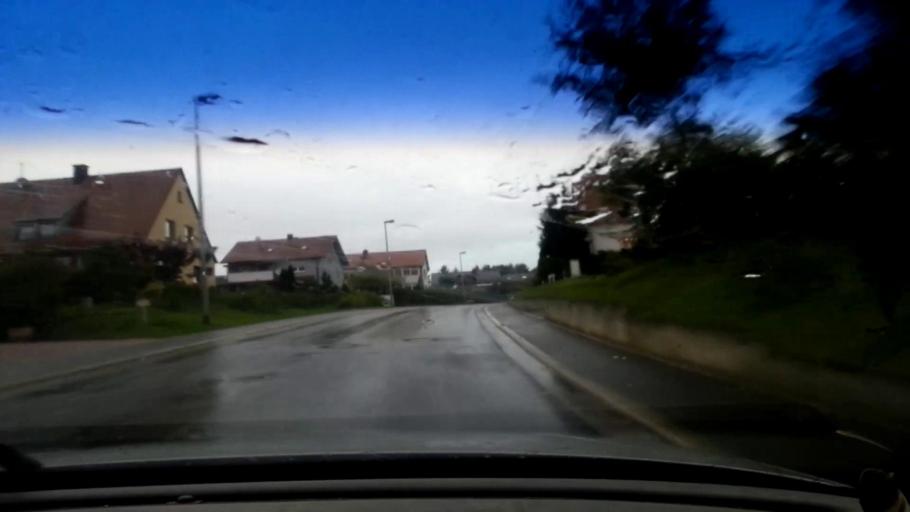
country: DE
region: Bavaria
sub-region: Upper Franconia
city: Walsdorf
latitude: 49.8727
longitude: 10.7801
